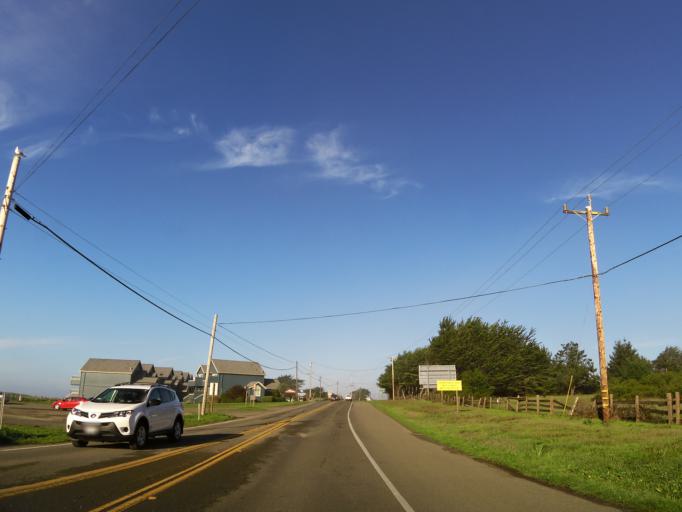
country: US
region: California
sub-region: Mendocino County
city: Fort Bragg
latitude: 39.4610
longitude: -123.8063
